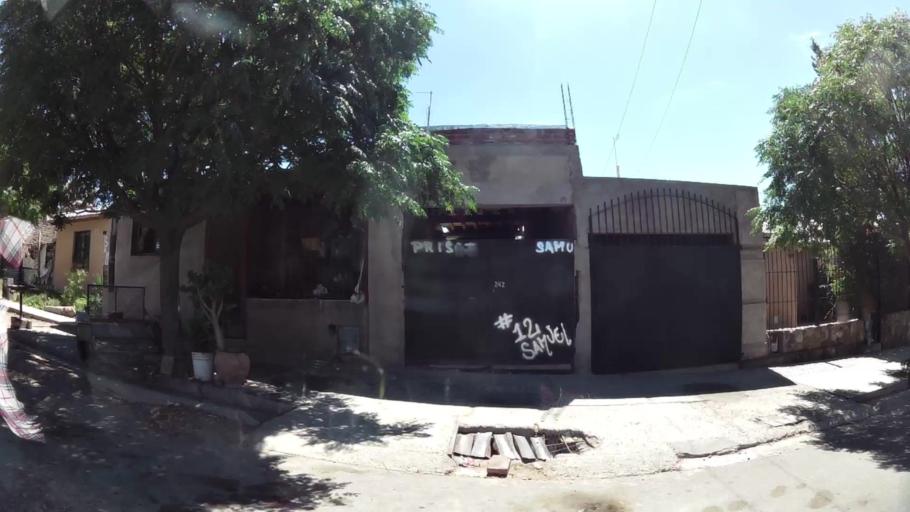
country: AR
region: Mendoza
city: Las Heras
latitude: -32.8507
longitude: -68.8727
